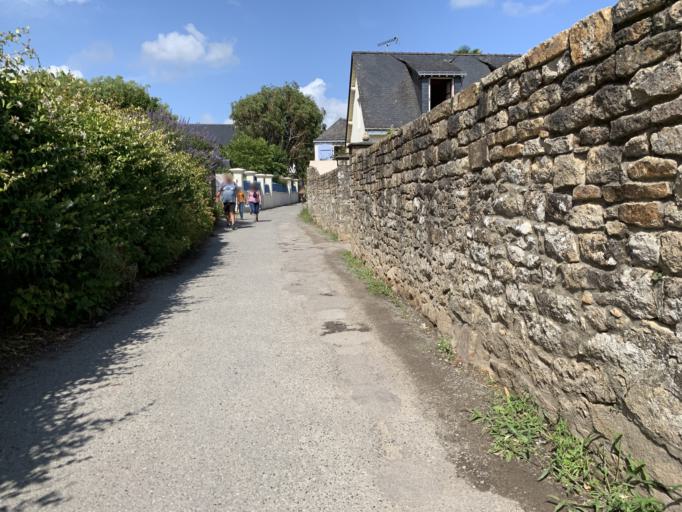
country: FR
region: Brittany
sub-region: Departement du Morbihan
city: Arradon
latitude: 47.5991
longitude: -2.8441
